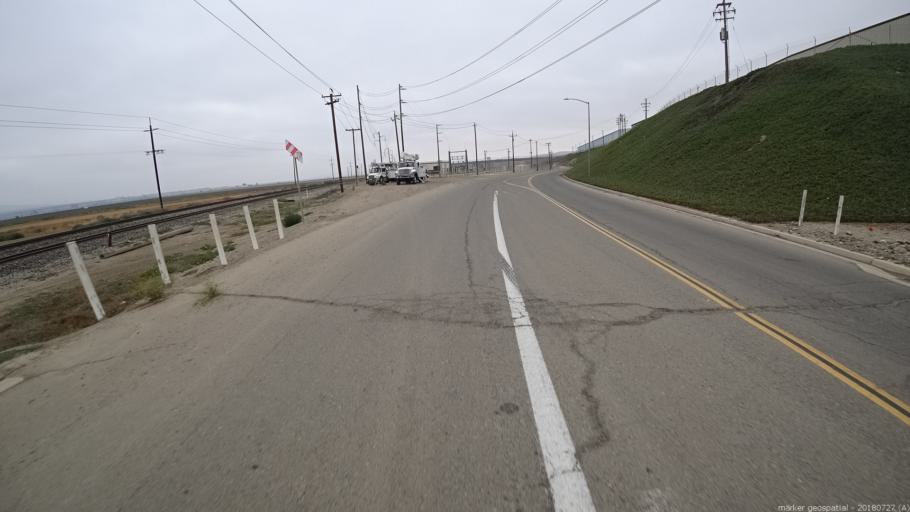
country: US
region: California
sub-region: Monterey County
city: King City
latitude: 36.2270
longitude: -121.1295
